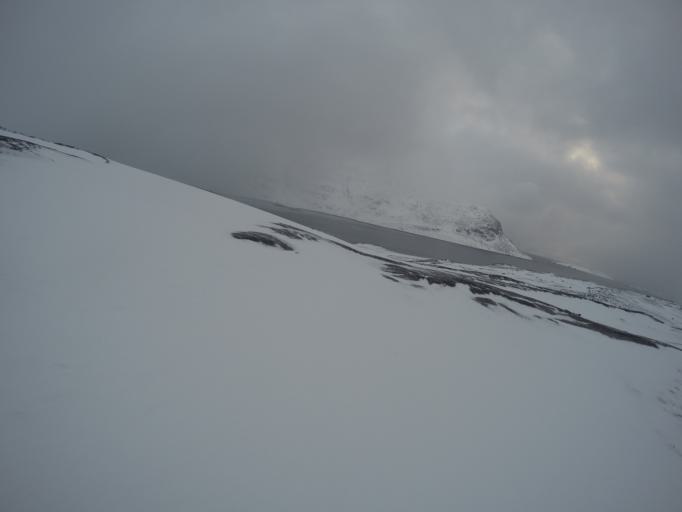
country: GL
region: Sermersooq
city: Nuuk
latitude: 64.1374
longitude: -51.6669
